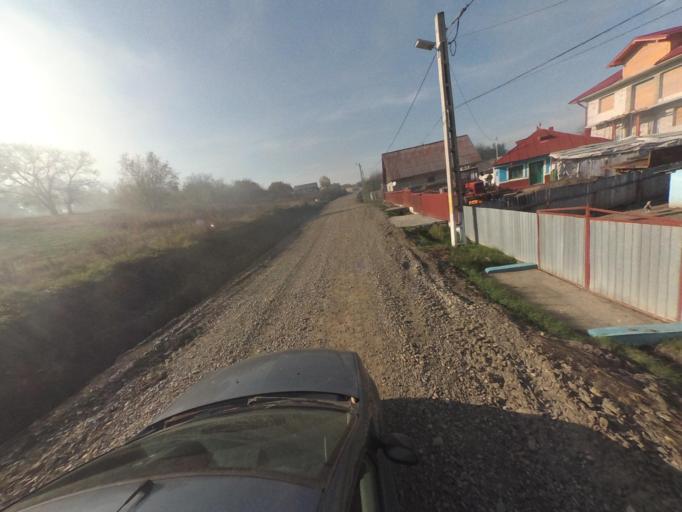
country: RO
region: Vaslui
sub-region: Comuna Bacesti
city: Bacesti
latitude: 46.8711
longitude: 27.2038
